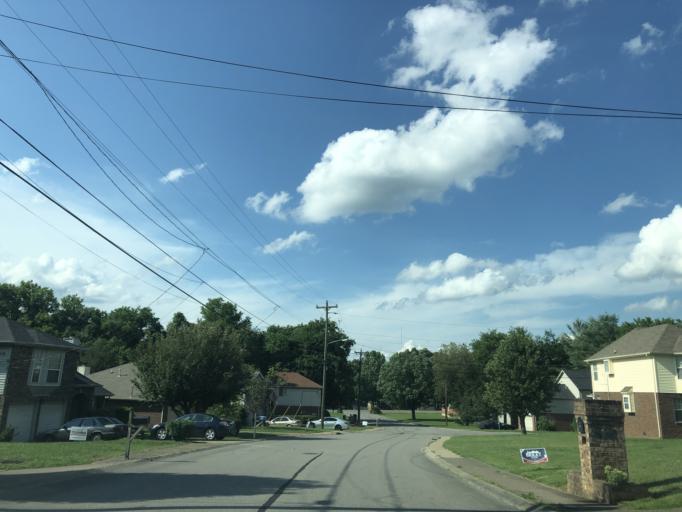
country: US
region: Tennessee
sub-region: Davidson County
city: Nashville
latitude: 36.2300
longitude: -86.8021
